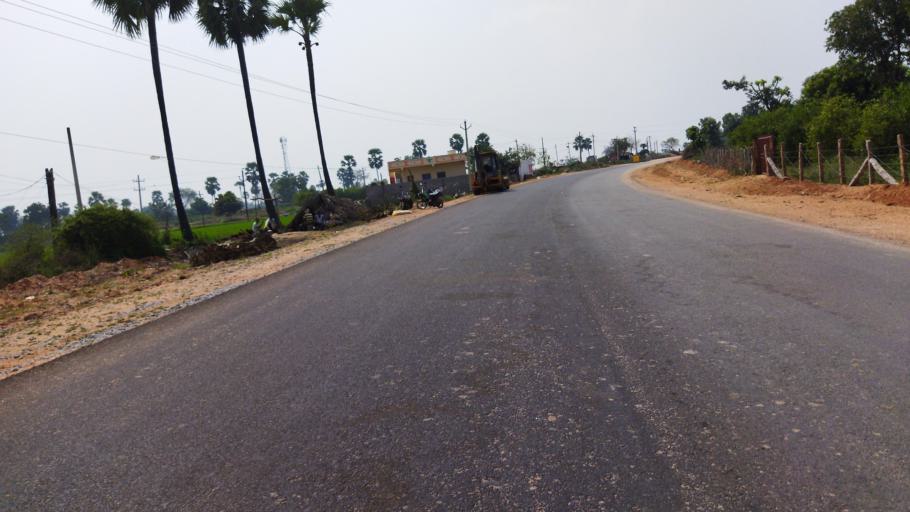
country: IN
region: Telangana
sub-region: Nalgonda
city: Nalgonda
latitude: 17.1121
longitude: 79.3593
